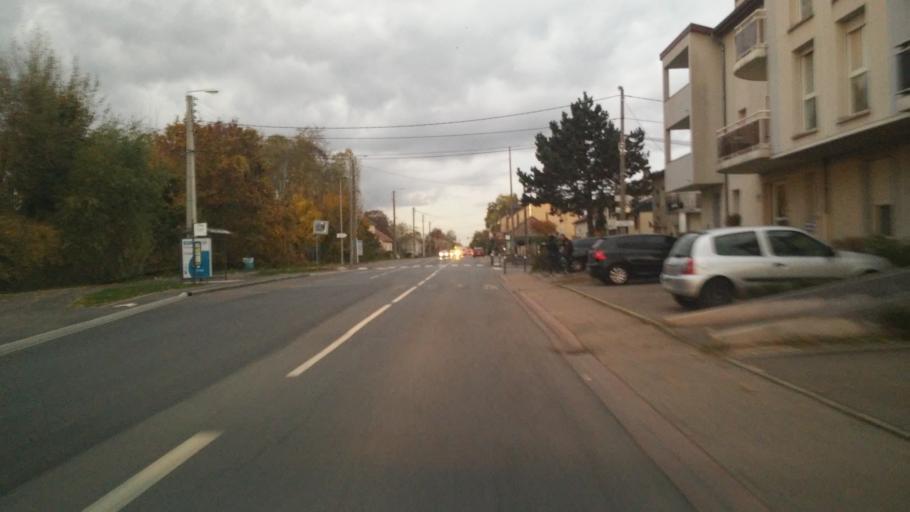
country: FR
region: Lorraine
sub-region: Departement de la Moselle
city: Talange
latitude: 49.2269
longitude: 6.1670
